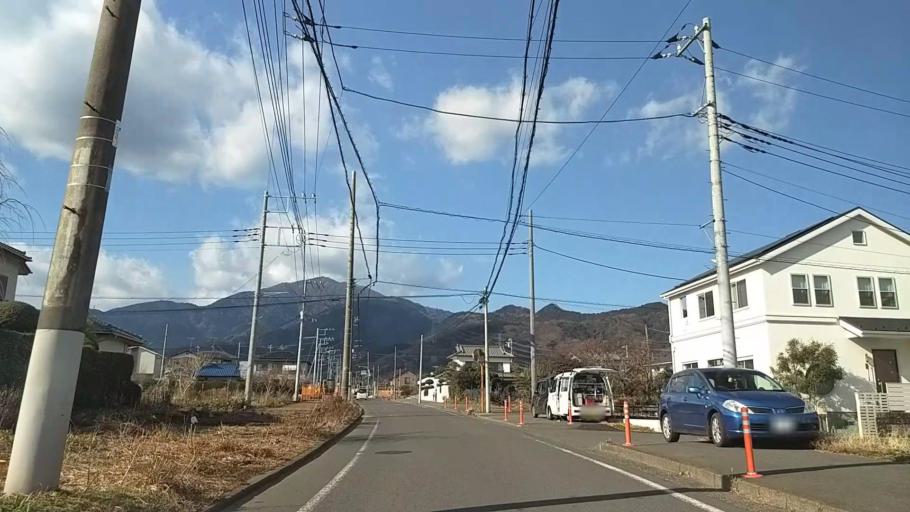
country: JP
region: Kanagawa
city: Isehara
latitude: 35.4107
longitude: 139.2891
